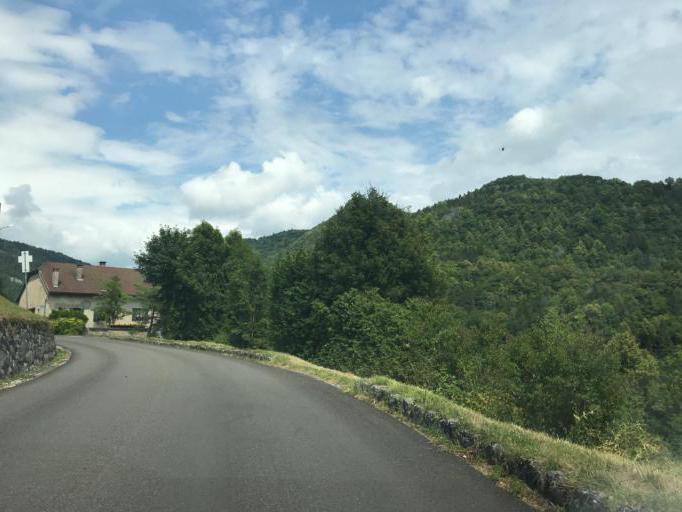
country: FR
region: Franche-Comte
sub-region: Departement du Jura
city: Saint-Claude
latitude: 46.4037
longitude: 5.8660
